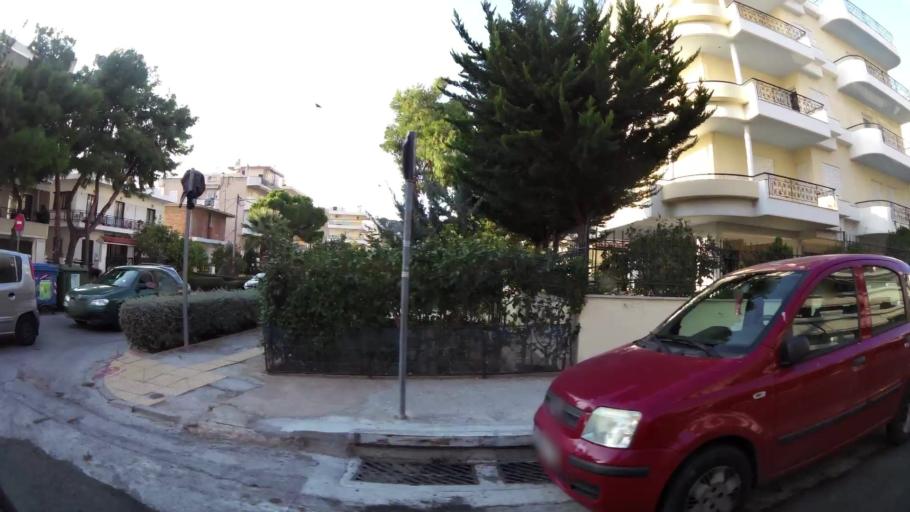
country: GR
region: Attica
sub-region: Nomarchia Athinas
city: Argyroupoli
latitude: 37.8982
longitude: 23.7662
